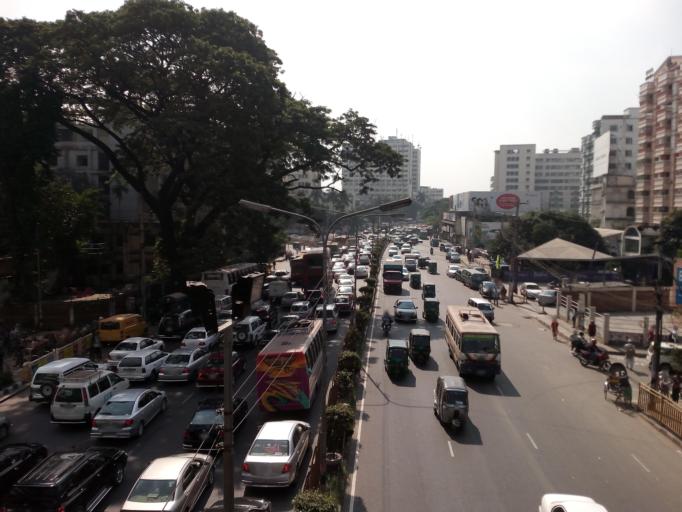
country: BD
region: Dhaka
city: Azimpur
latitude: 23.7429
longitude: 90.3957
